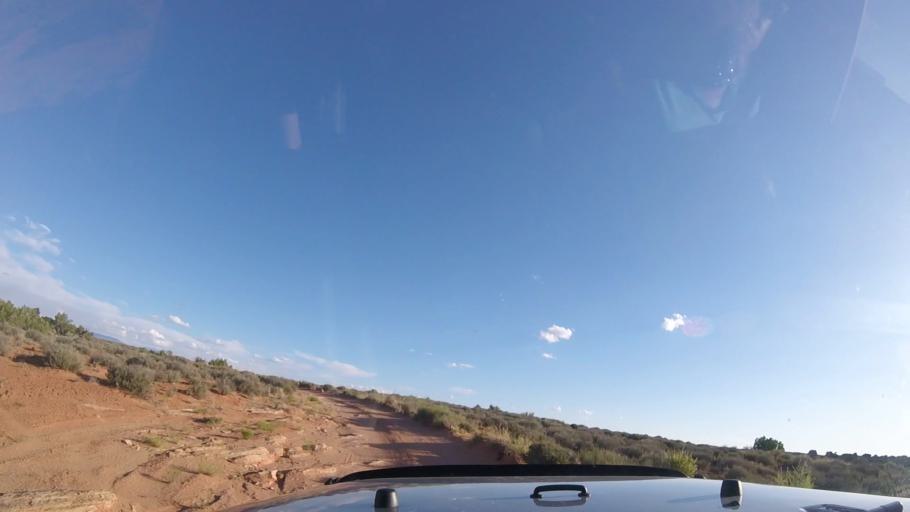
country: US
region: Utah
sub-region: Grand County
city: Moab
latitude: 38.2071
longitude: -109.7862
